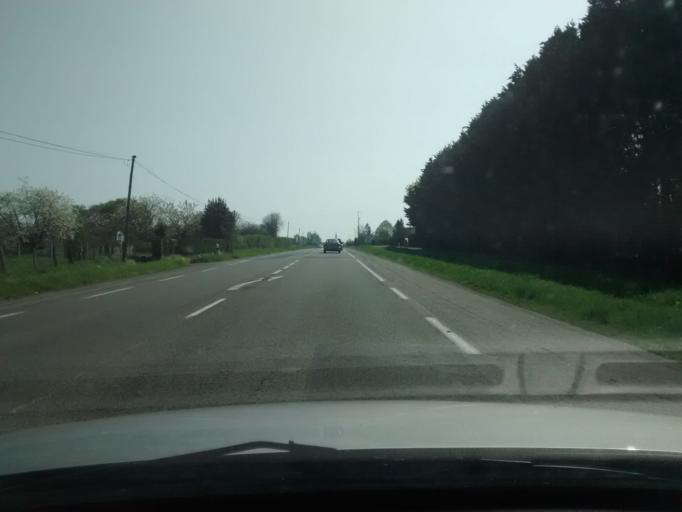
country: FR
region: Pays de la Loire
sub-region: Departement de la Mayenne
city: Soulge-sur-Ouette
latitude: 48.0611
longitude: -0.5830
